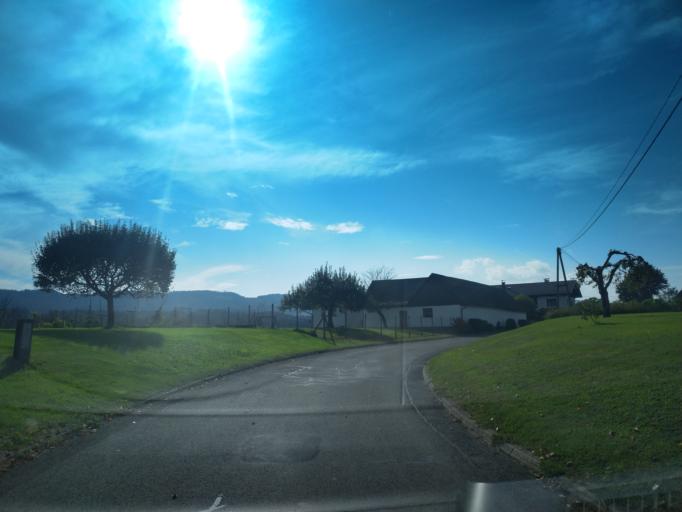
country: AT
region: Styria
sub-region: Politischer Bezirk Leibnitz
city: Sankt Johann im Saggautal
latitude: 46.6990
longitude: 15.3837
